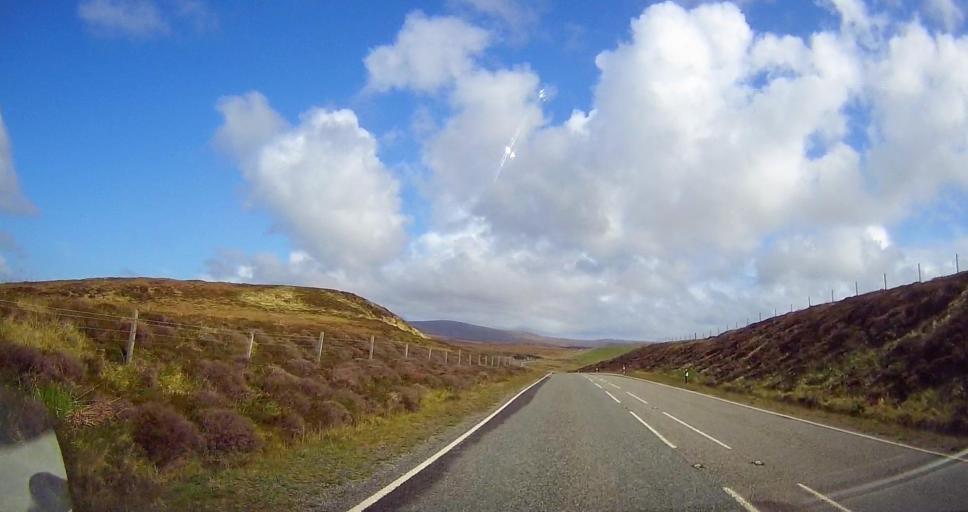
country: GB
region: Scotland
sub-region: Shetland Islands
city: Lerwick
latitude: 60.4693
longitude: -1.4070
